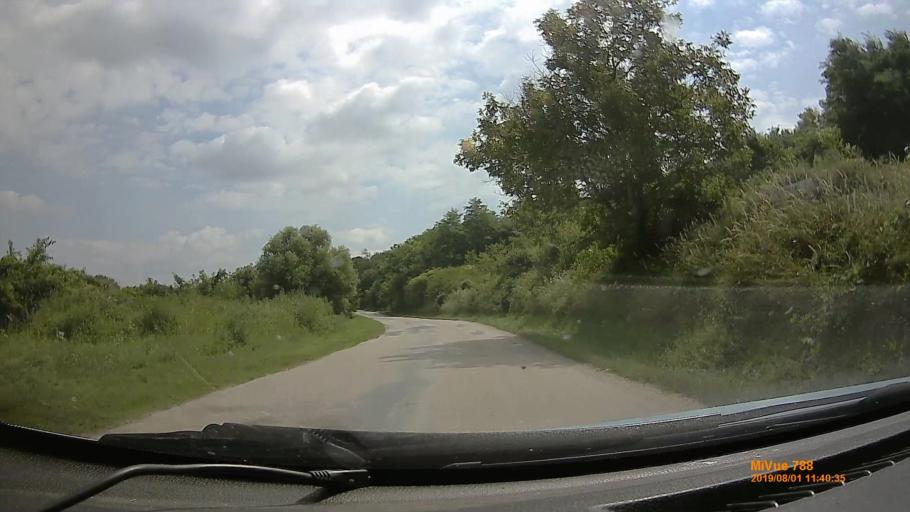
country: HU
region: Baranya
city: Villany
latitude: 45.8908
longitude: 18.3956
